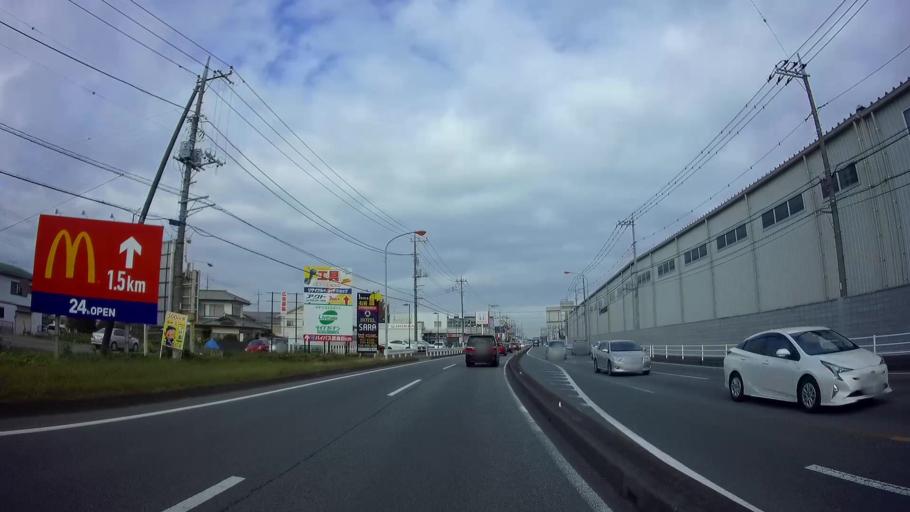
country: JP
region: Saitama
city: Konosu
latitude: 36.0708
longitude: 139.5011
